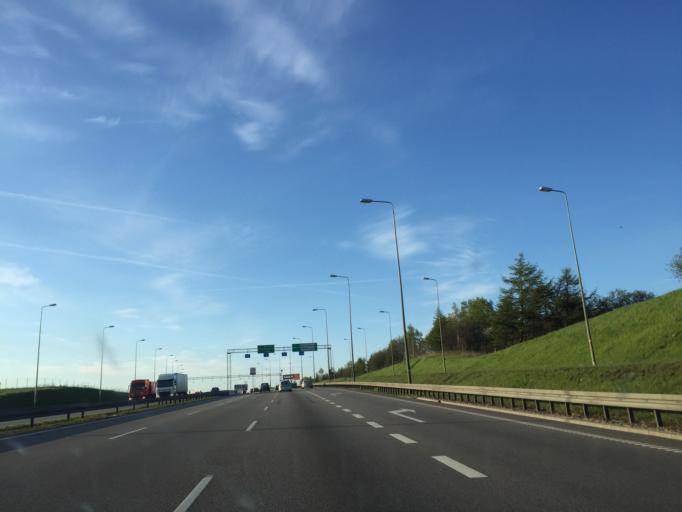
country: PL
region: Pomeranian Voivodeship
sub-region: Powiat gdanski
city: Kowale
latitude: 54.3620
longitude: 18.5199
